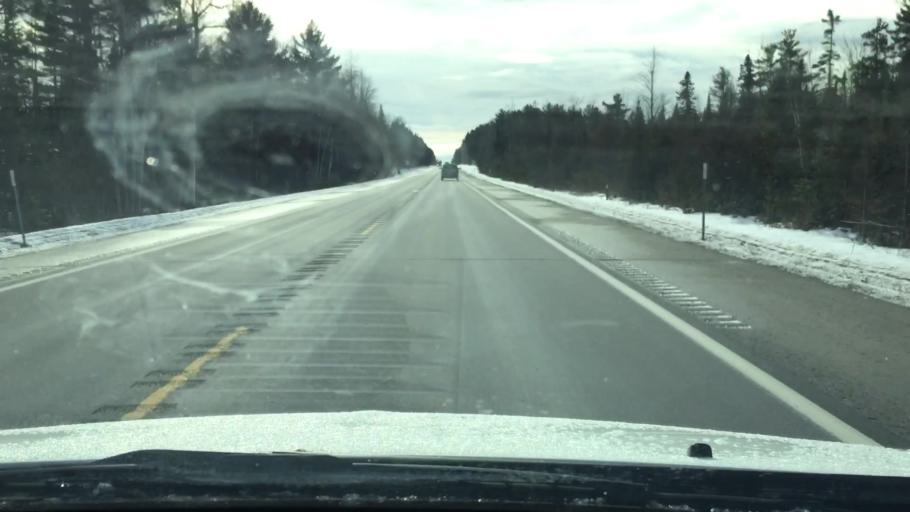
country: US
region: Michigan
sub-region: Kalkaska County
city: Kalkaska
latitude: 44.6988
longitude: -85.2058
